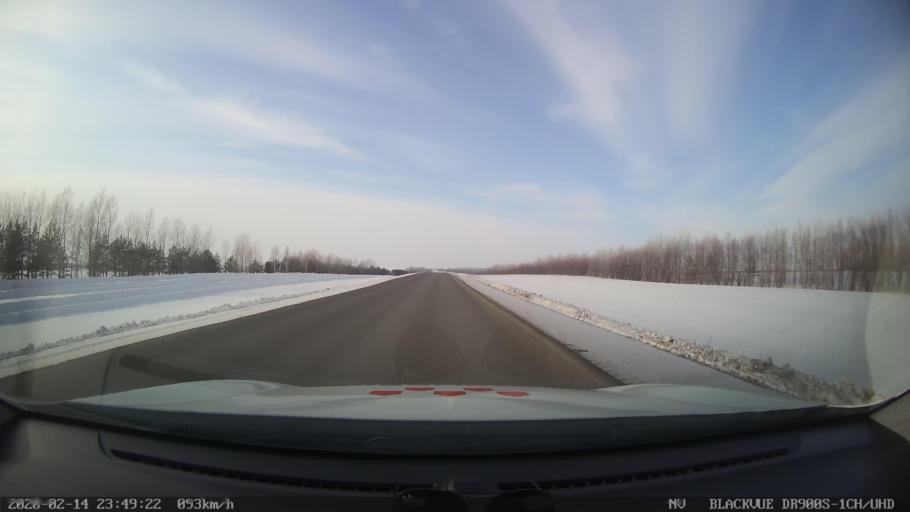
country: RU
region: Tatarstan
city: Kuybyshevskiy Zaton
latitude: 55.2532
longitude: 49.1837
